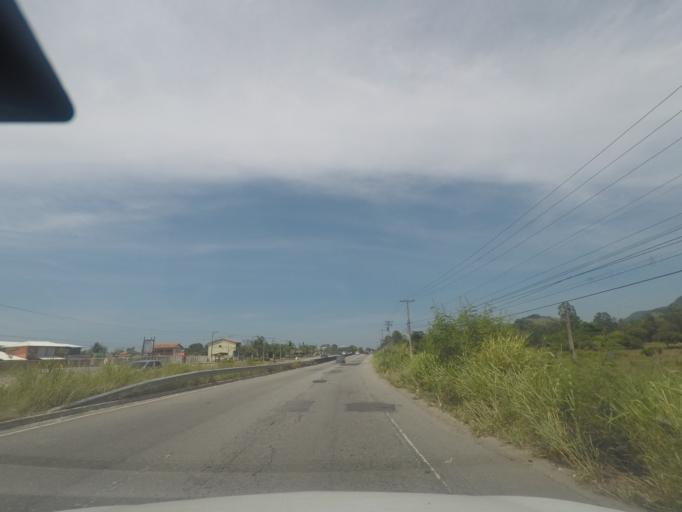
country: BR
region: Rio de Janeiro
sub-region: Marica
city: Marica
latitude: -22.9154
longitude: -42.8487
